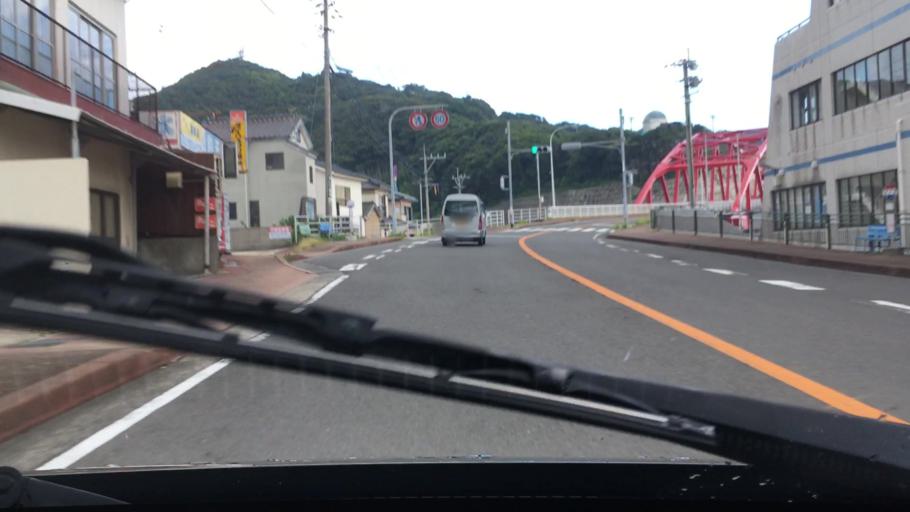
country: JP
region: Nagasaki
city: Togitsu
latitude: 32.8805
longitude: 129.6799
